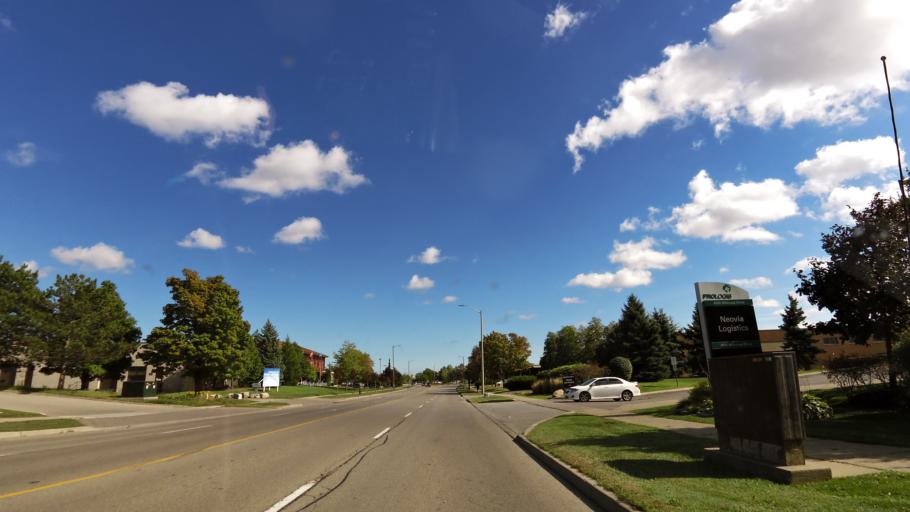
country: CA
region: Ontario
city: Mississauga
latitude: 43.5920
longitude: -79.7455
